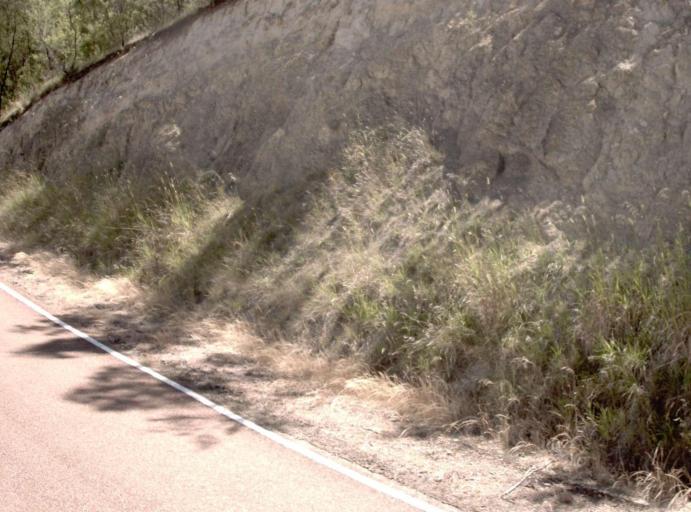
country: AU
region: Victoria
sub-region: East Gippsland
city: Lakes Entrance
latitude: -37.4795
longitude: 148.1818
